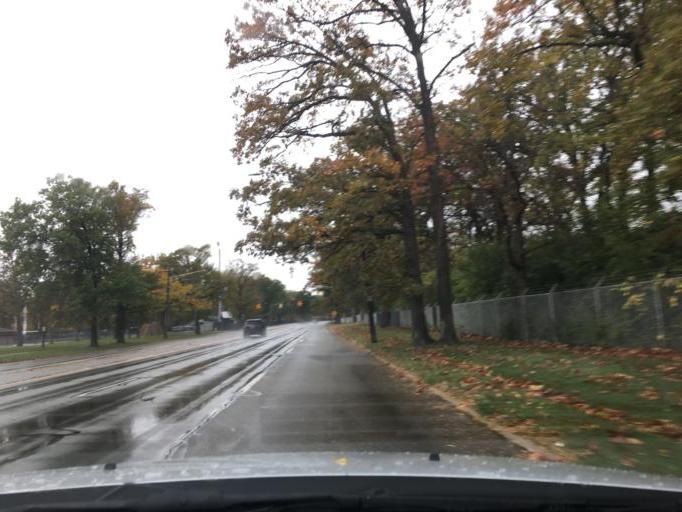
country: US
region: Michigan
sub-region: Wayne County
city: Allen Park
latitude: 42.2915
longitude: -83.2350
